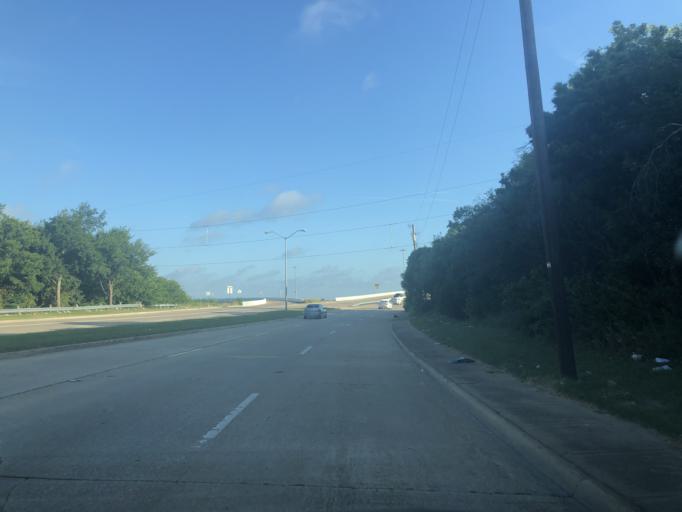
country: US
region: Texas
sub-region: Dallas County
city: Duncanville
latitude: 32.6679
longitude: -96.9464
